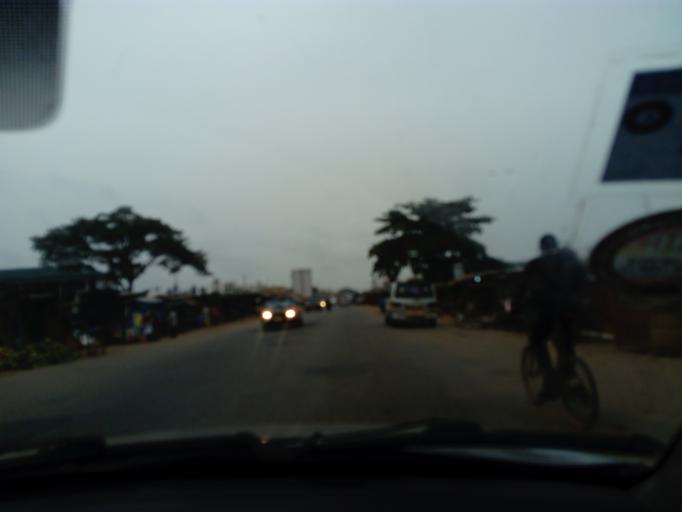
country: GH
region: Central
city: Cape Coast
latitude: 5.1341
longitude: -1.2771
